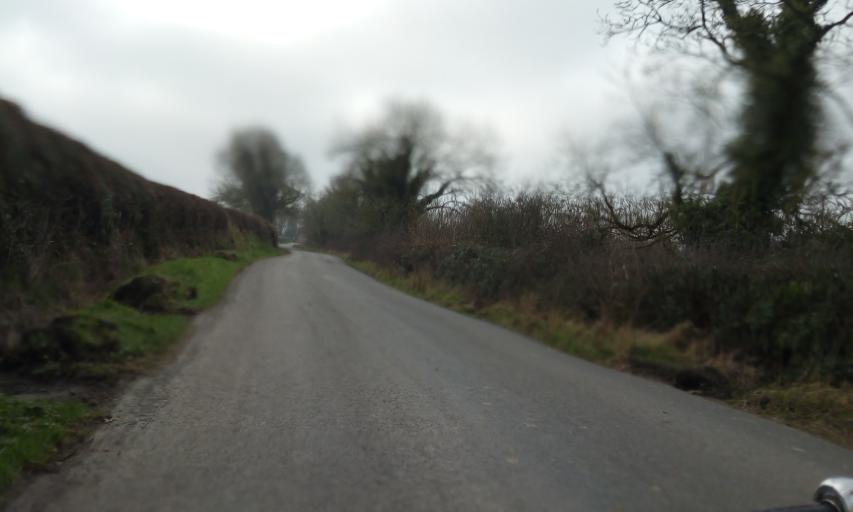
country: IE
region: Leinster
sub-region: Kilkenny
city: Kilkenny
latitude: 52.6628
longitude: -7.1882
